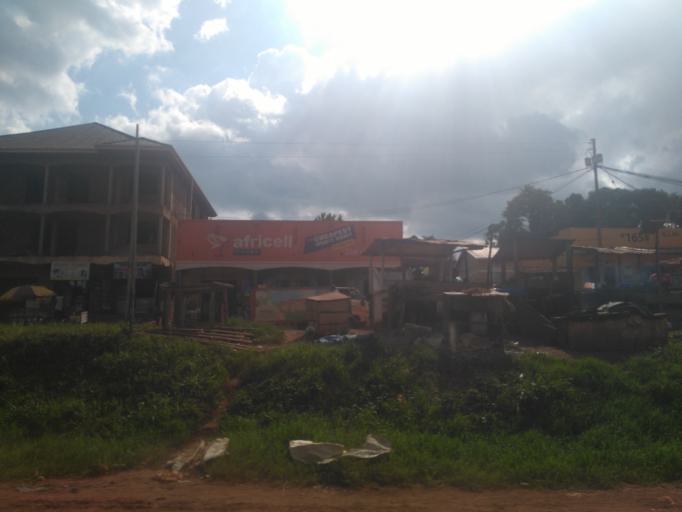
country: UG
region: Central Region
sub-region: Wakiso District
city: Kajansi
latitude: 0.2725
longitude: 32.4617
